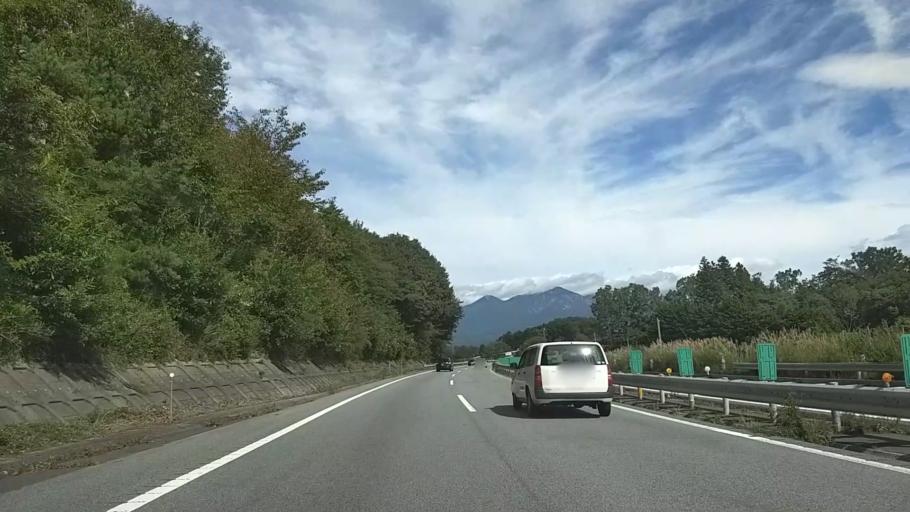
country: JP
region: Yamanashi
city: Nirasaki
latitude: 35.7963
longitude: 138.3961
